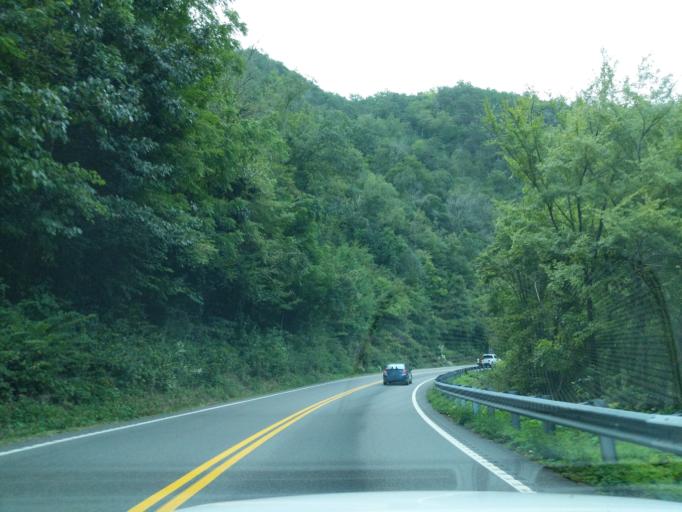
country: US
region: Georgia
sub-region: Fannin County
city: McCaysville
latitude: 35.0801
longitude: -84.5068
